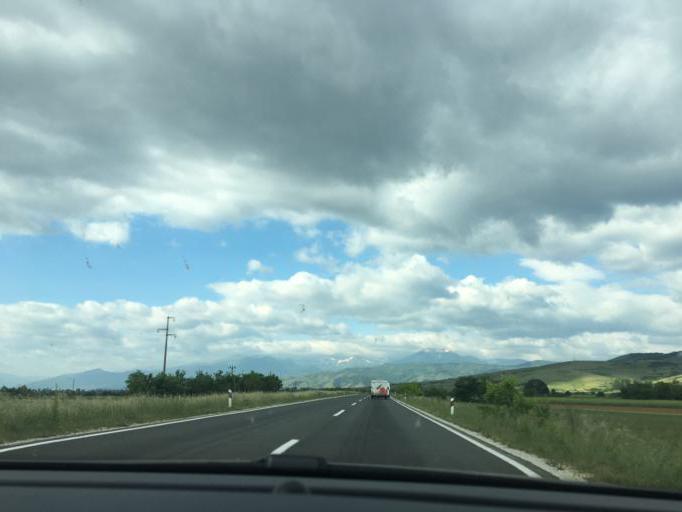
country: MK
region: Mogila
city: Beranci
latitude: 41.1578
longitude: 21.3782
